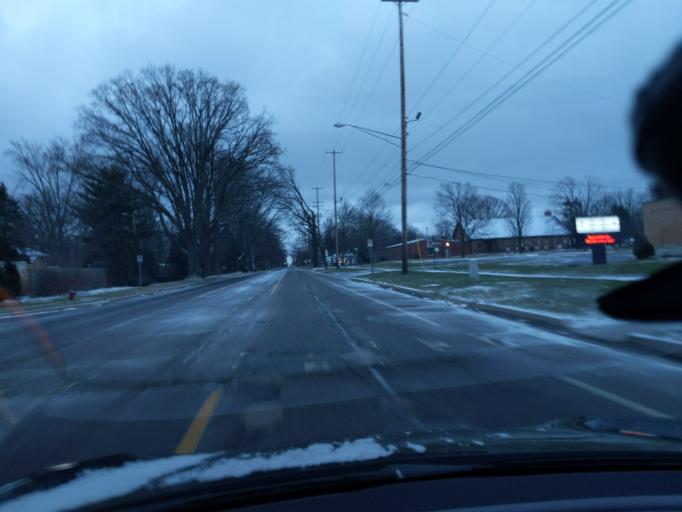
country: US
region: Michigan
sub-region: Ingham County
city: Edgemont Park
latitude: 42.7121
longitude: -84.5912
